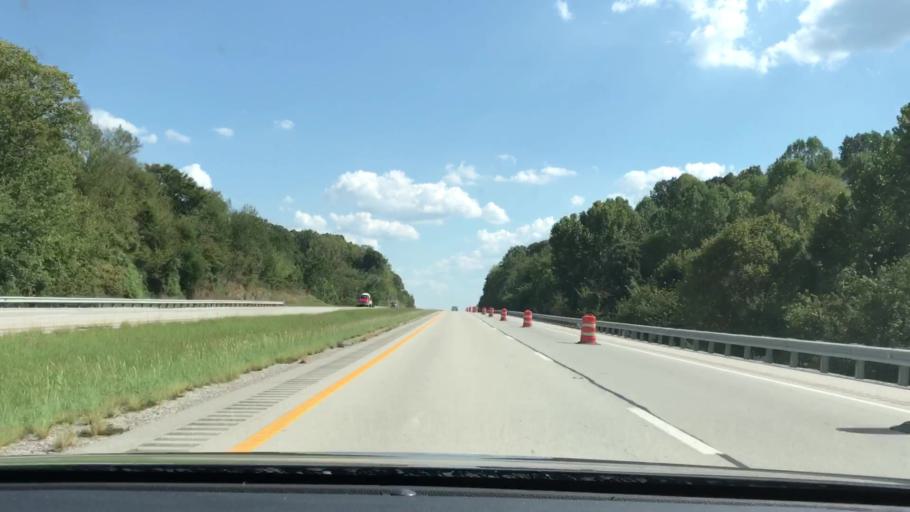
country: US
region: Kentucky
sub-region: Butler County
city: Morgantown
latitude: 37.2288
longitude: -86.7242
